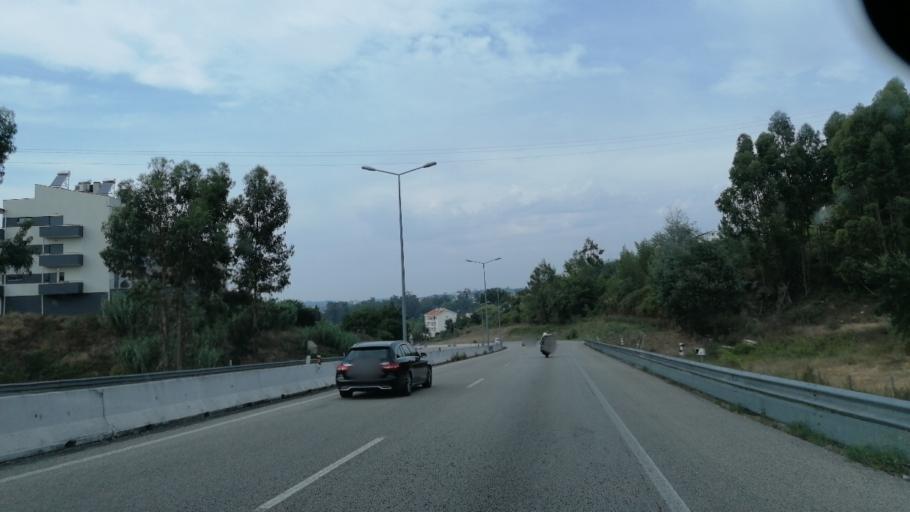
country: PT
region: Coimbra
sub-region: Coimbra
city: Coimbra
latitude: 40.2093
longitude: -8.4467
